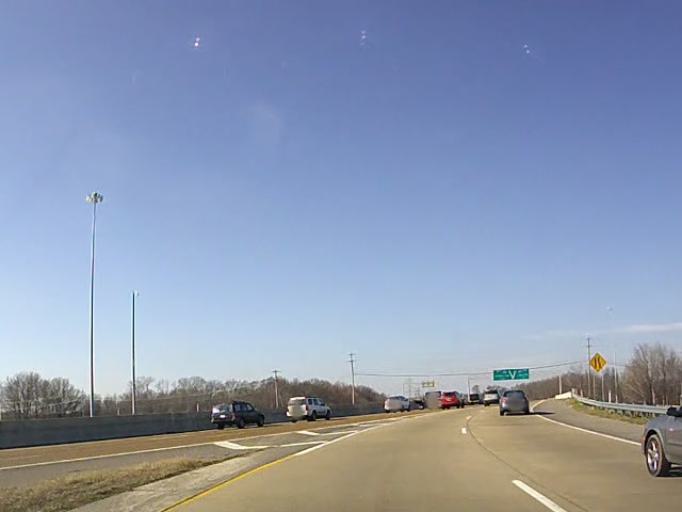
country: US
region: Tennessee
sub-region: Shelby County
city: Germantown
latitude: 35.0745
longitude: -89.8605
